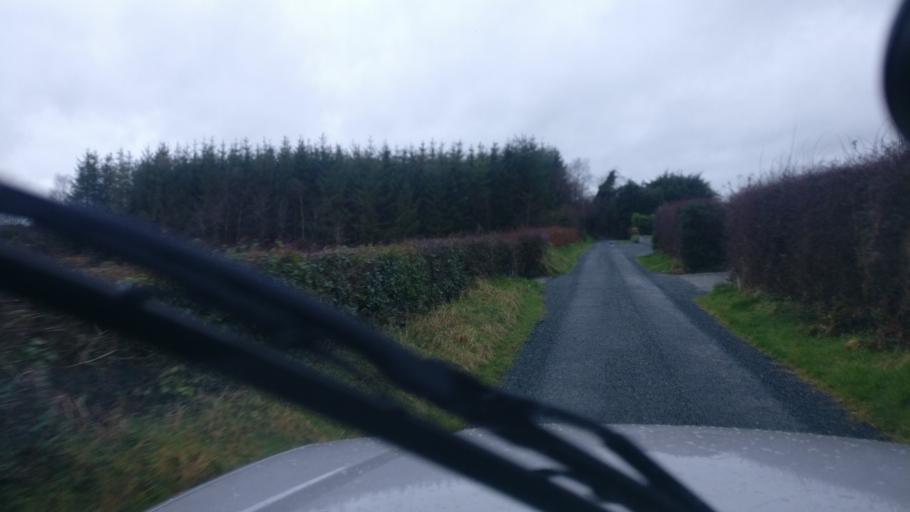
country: IE
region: Connaught
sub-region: County Galway
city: Ballinasloe
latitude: 53.2527
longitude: -8.3626
